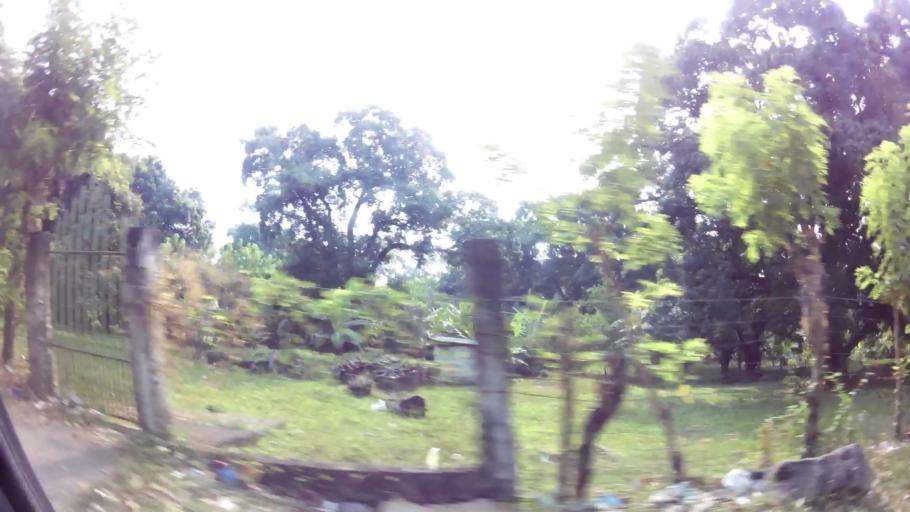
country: HN
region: Cortes
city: El Zapotal del Norte
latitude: 15.5186
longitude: -88.0500
